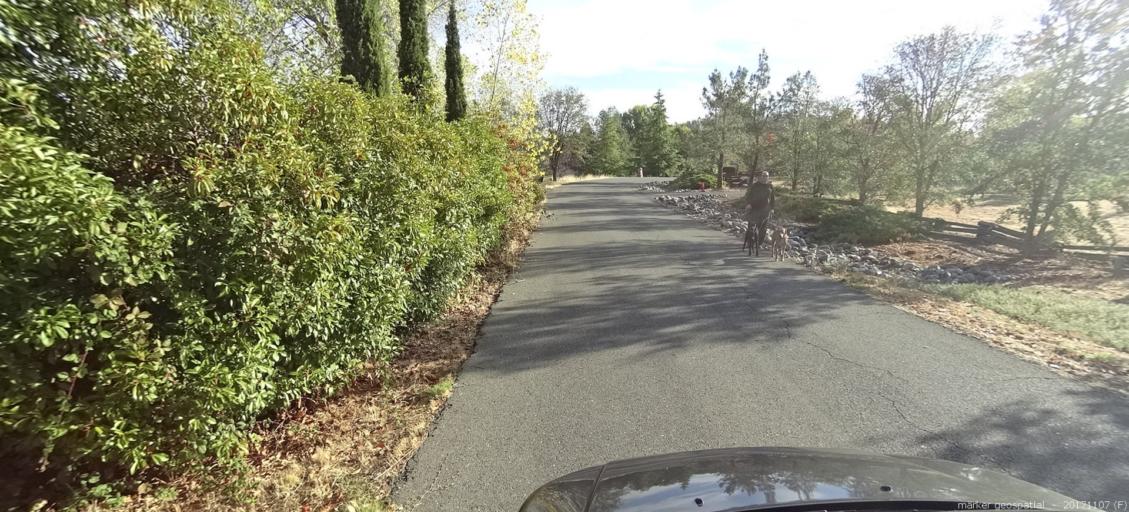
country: US
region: California
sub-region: Shasta County
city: Shasta
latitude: 40.5444
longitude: -122.4626
